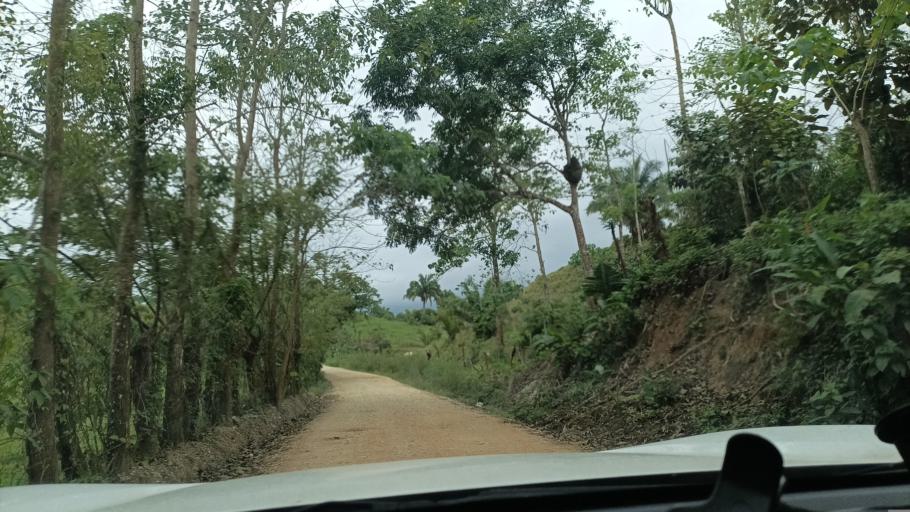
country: MX
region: Veracruz
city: Hidalgotitlan
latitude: 17.6309
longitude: -94.5105
